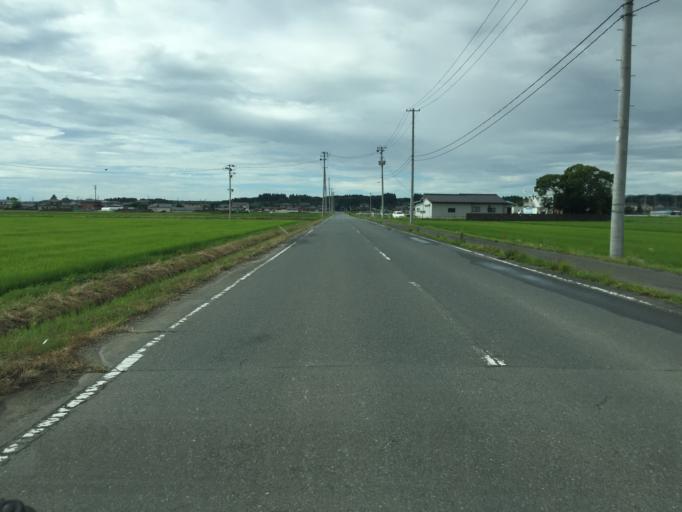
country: JP
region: Miyagi
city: Marumori
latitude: 37.7914
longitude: 140.9571
